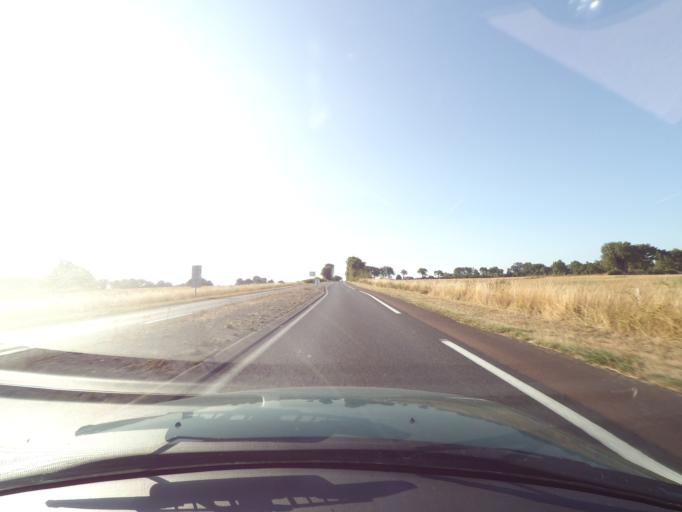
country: FR
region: Poitou-Charentes
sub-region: Departement des Deux-Sevres
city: Chiche
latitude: 46.7790
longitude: -0.3303
